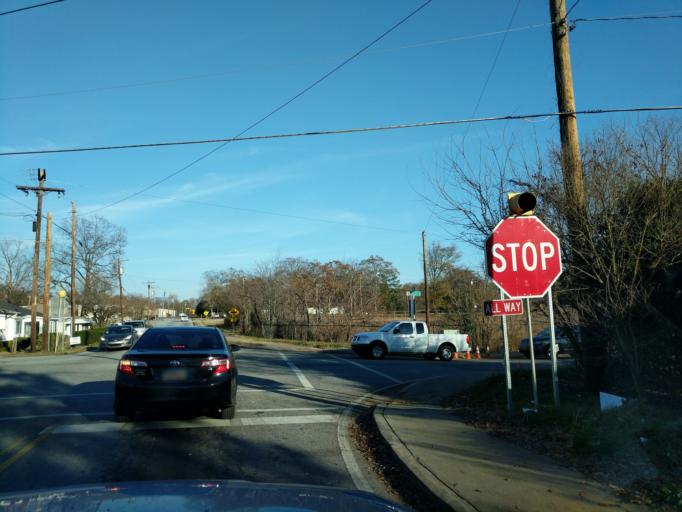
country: US
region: South Carolina
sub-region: Spartanburg County
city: Saxon
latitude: 34.9637
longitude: -81.9688
